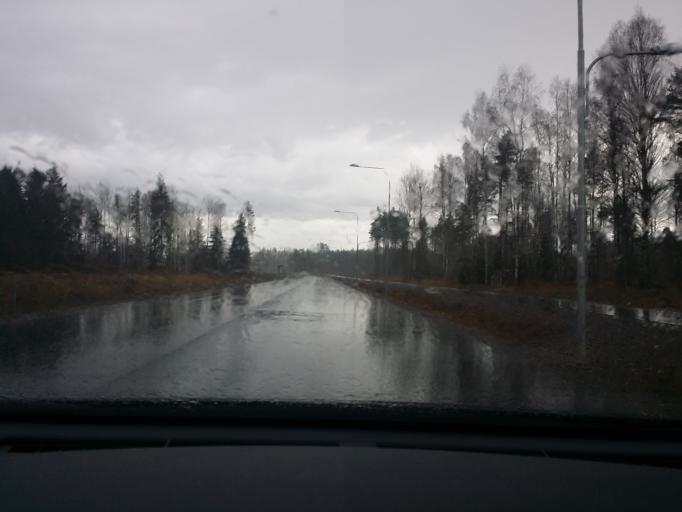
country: SE
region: Soedermanland
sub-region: Eskilstuna Kommun
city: Arla
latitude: 59.3600
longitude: 16.7002
